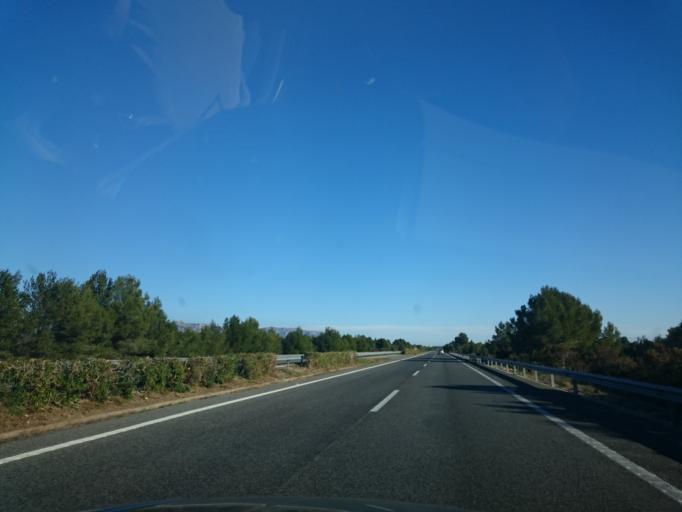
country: ES
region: Catalonia
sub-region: Provincia de Tarragona
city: l'Ametlla de Mar
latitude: 40.8662
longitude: 0.7769
